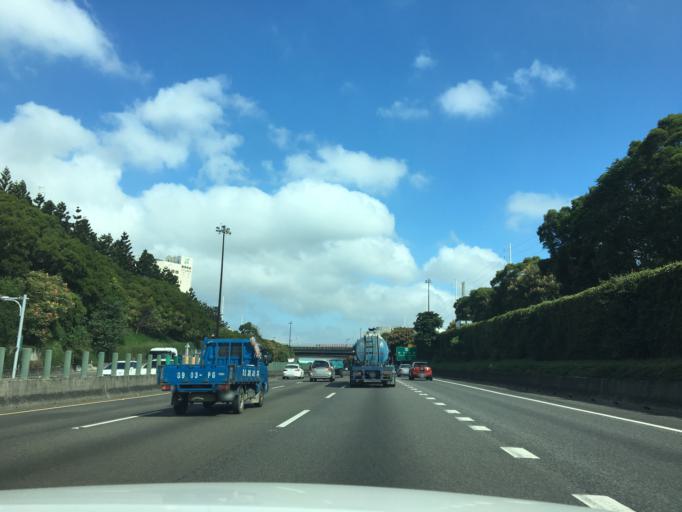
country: TW
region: Taiwan
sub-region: Hsinchu
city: Hsinchu
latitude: 24.7727
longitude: 121.0036
